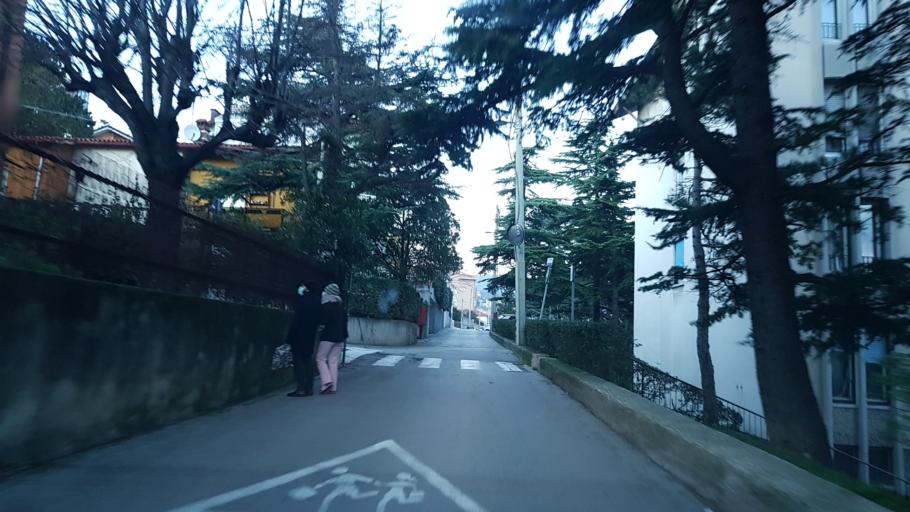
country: IT
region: Friuli Venezia Giulia
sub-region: Provincia di Trieste
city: Trieste
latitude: 45.6268
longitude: 13.7913
